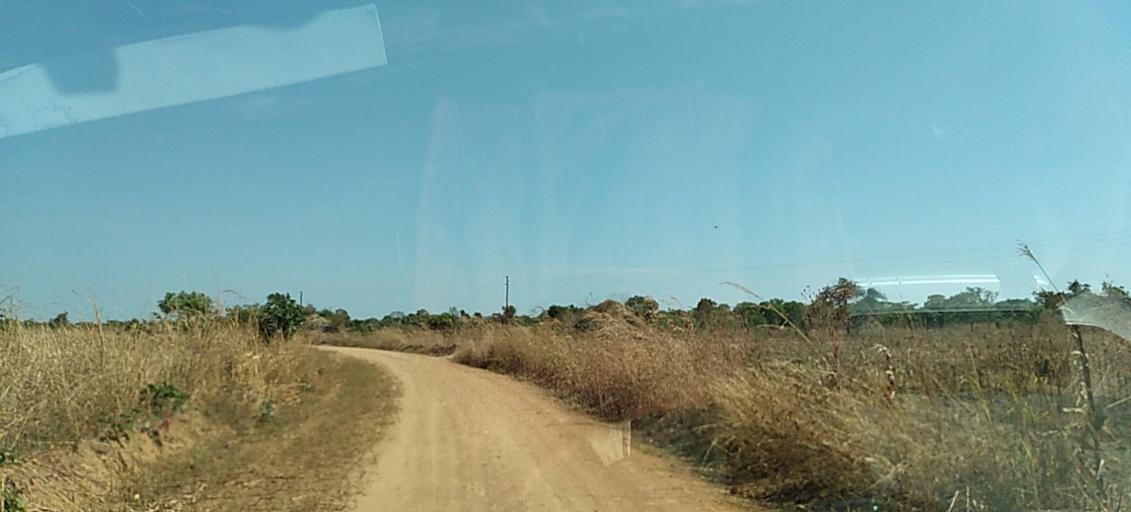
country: ZM
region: Copperbelt
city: Chililabombwe
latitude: -12.3522
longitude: 27.8832
